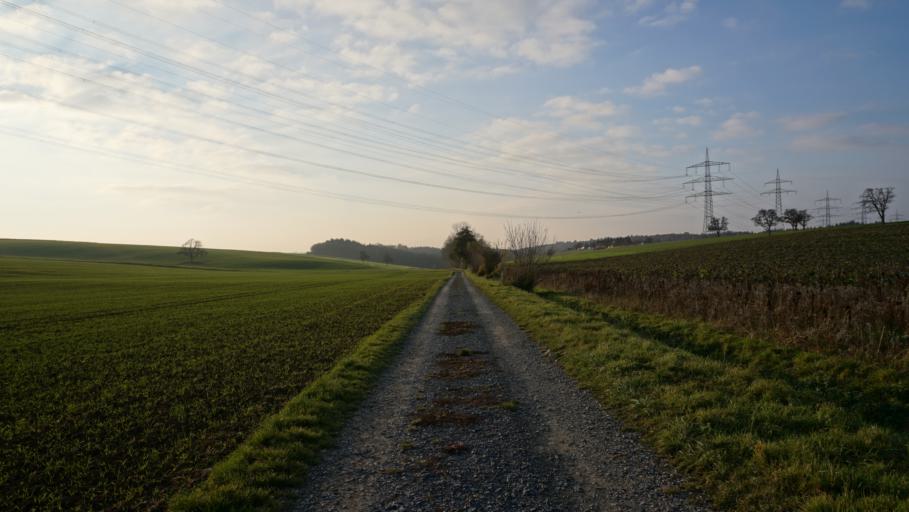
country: DE
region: Baden-Wuerttemberg
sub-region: Karlsruhe Region
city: Huffenhardt
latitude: 49.3032
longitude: 9.0741
